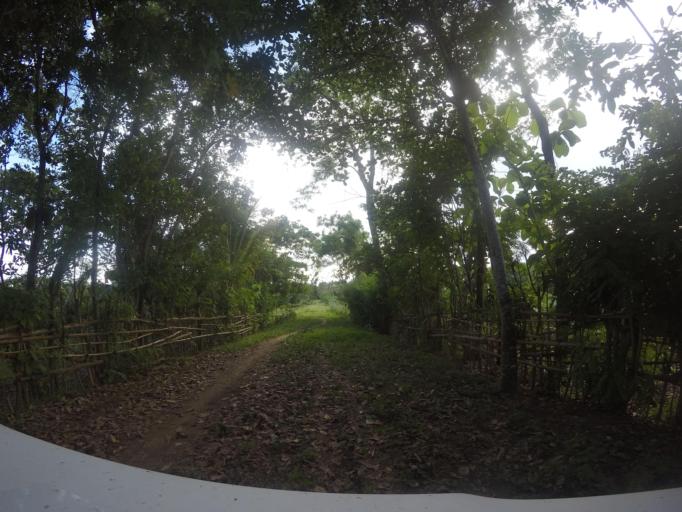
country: TL
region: Lautem
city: Lospalos
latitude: -8.5139
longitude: 126.9925
